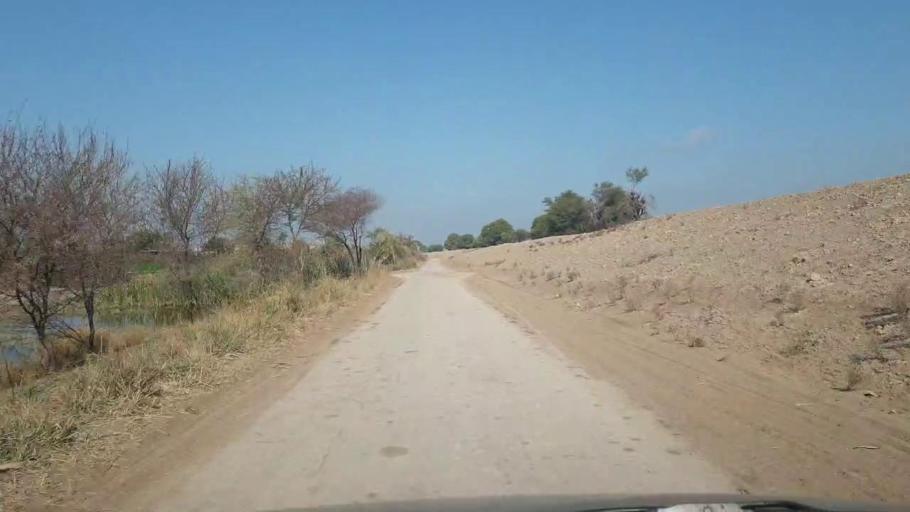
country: PK
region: Sindh
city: Shahdadpur
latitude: 25.8791
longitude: 68.5466
